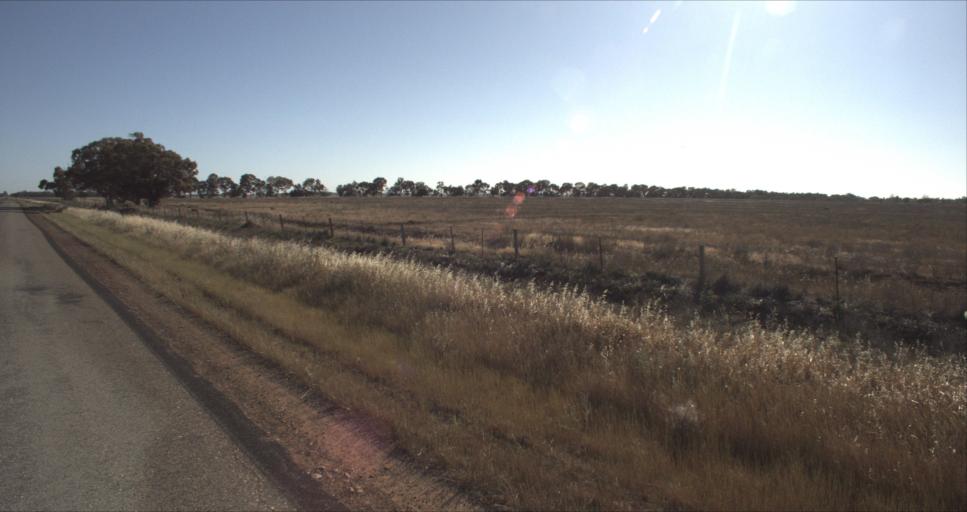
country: AU
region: New South Wales
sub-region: Leeton
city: Leeton
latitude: -34.5809
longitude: 146.2616
